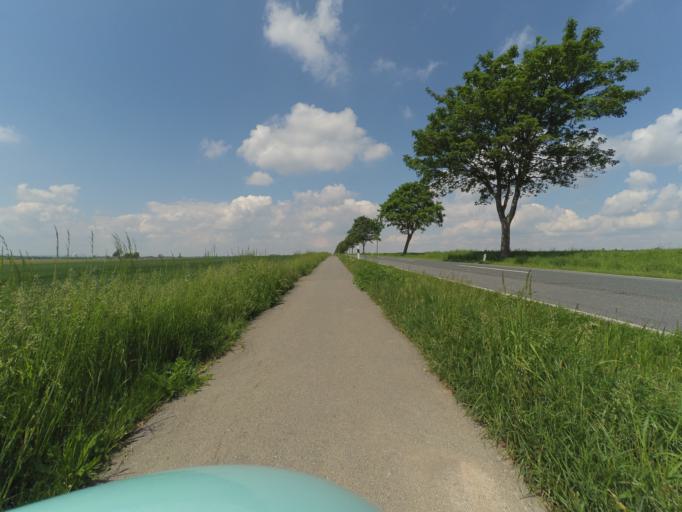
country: DE
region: Lower Saxony
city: Hohenhameln
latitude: 52.2504
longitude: 10.0996
